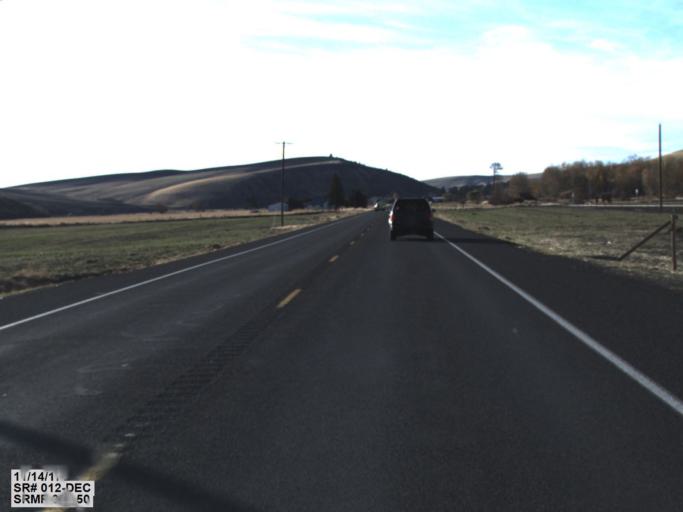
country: US
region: Washington
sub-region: Columbia County
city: Dayton
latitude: 46.2880
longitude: -118.0402
